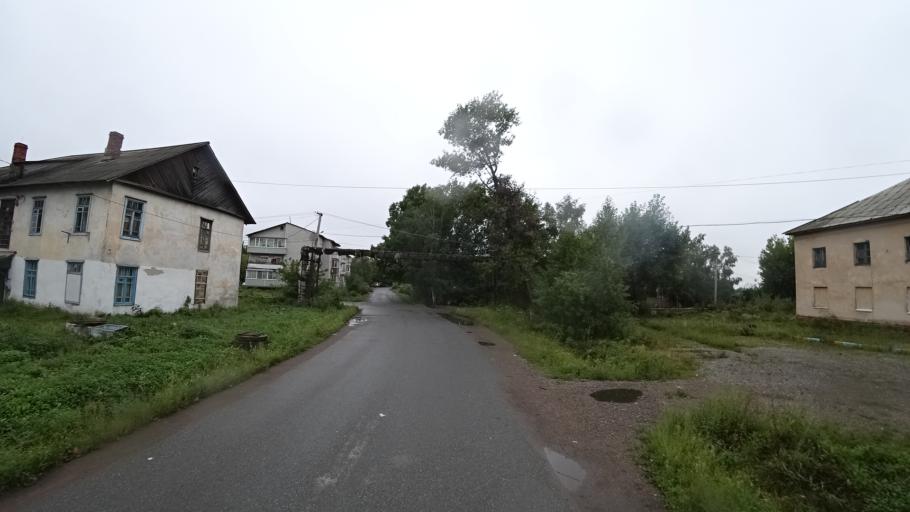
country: RU
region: Primorskiy
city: Monastyrishche
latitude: 44.1953
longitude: 132.4248
